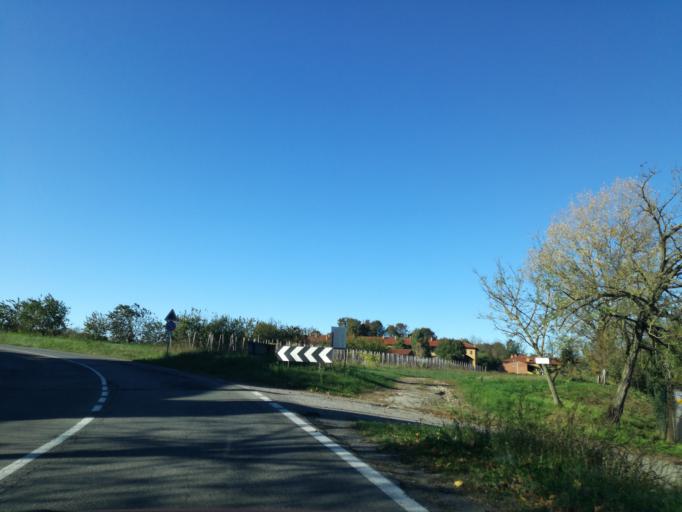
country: IT
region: Lombardy
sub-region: Provincia di Monza e Brianza
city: Macherio
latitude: 45.6389
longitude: 9.2907
